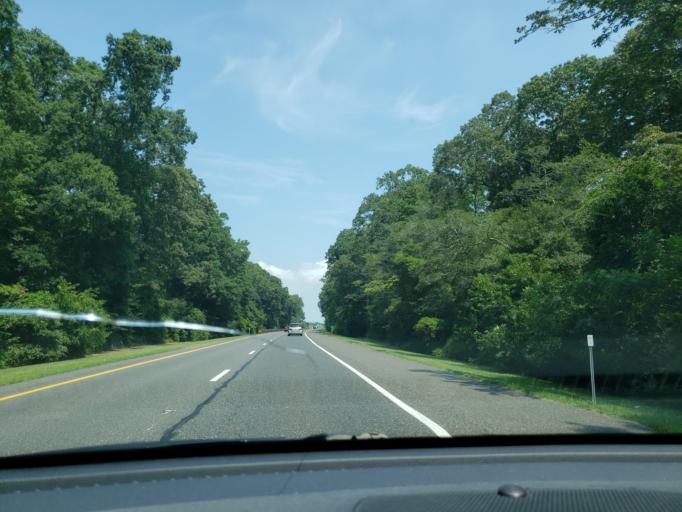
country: US
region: New Jersey
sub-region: Cape May County
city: Rio Grande
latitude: 38.9975
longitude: -74.8761
